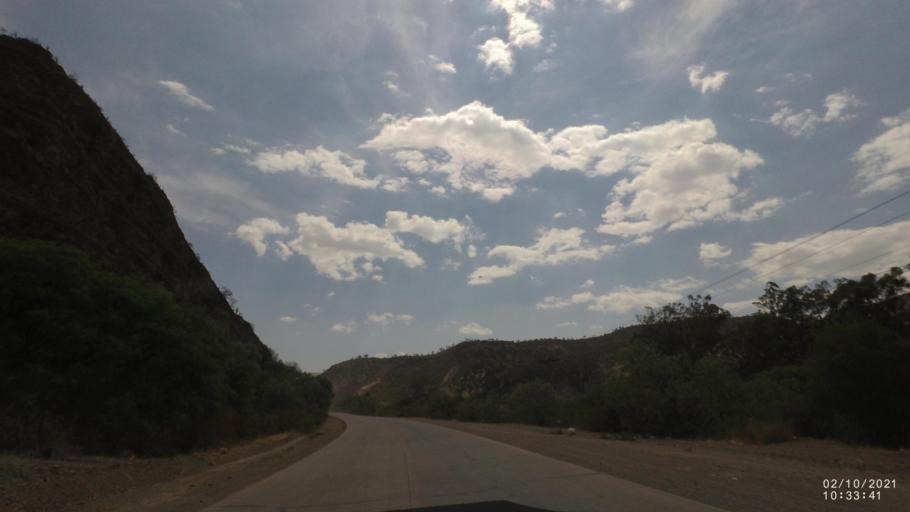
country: BO
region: Cochabamba
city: Capinota
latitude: -17.6796
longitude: -66.2509
